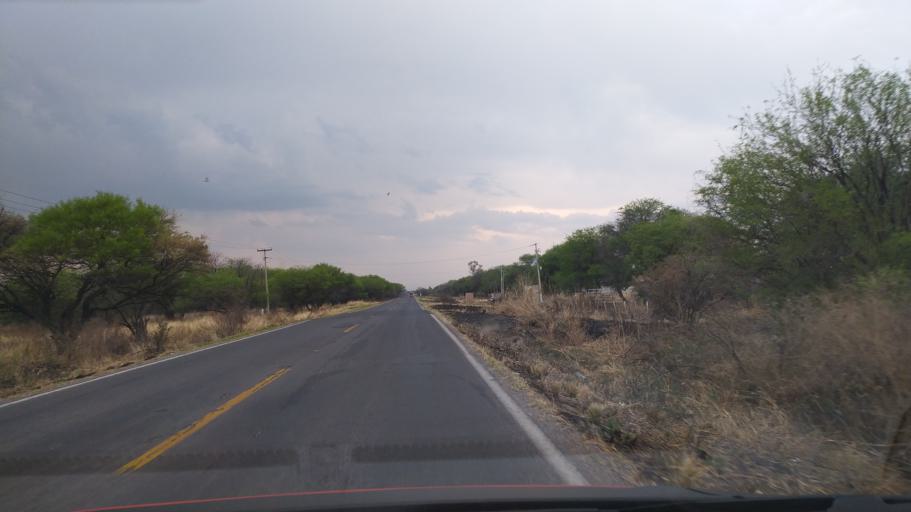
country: MX
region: Guanajuato
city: Ciudad Manuel Doblado
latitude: 20.7656
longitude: -101.9146
